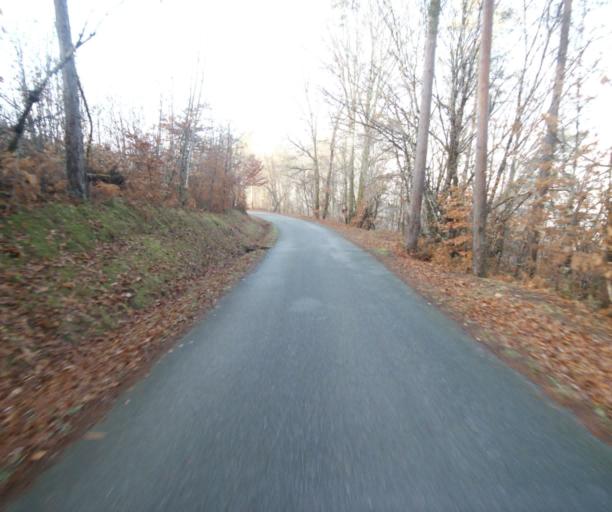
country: FR
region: Limousin
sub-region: Departement de la Correze
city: Laguenne
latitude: 45.2619
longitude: 1.7939
